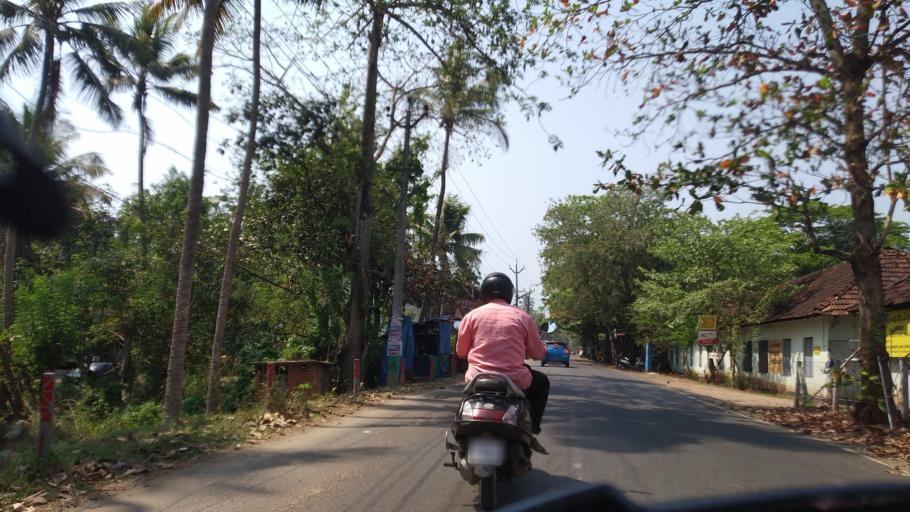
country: IN
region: Kerala
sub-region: Thrissur District
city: Kodungallur
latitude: 10.2218
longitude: 76.1581
